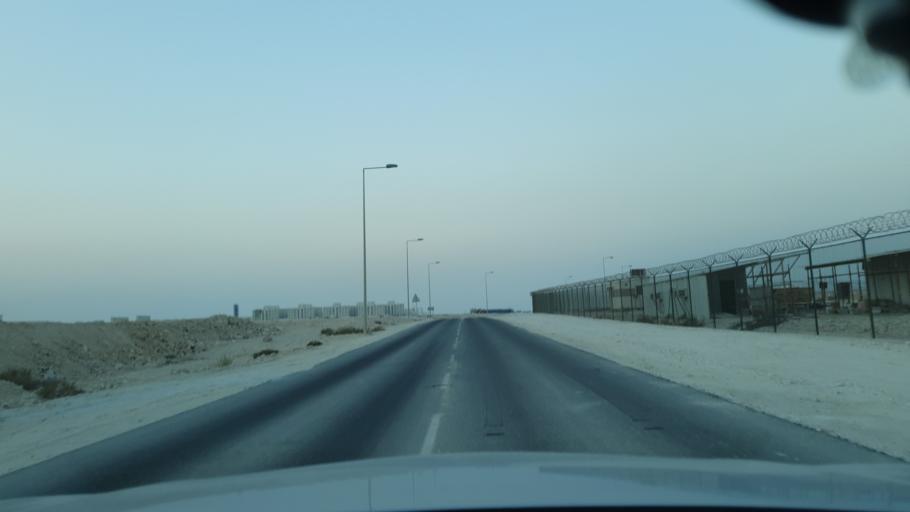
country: BH
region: Central Governorate
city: Dar Kulayb
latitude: 25.9745
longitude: 50.6095
